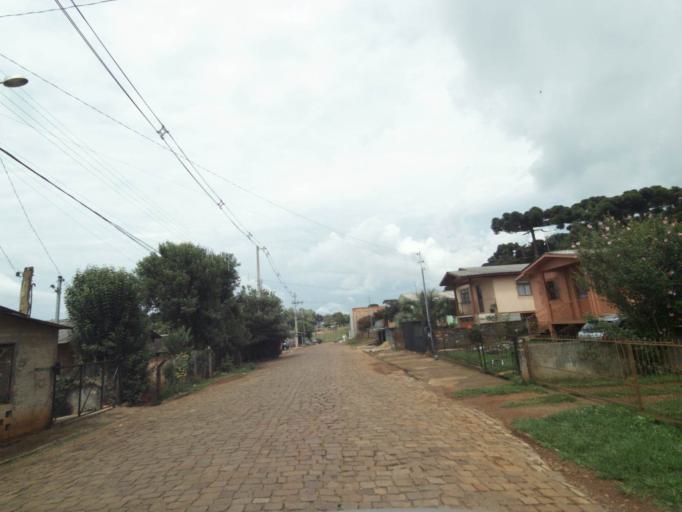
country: BR
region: Rio Grande do Sul
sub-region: Lagoa Vermelha
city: Lagoa Vermelha
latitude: -28.2251
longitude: -51.5140
